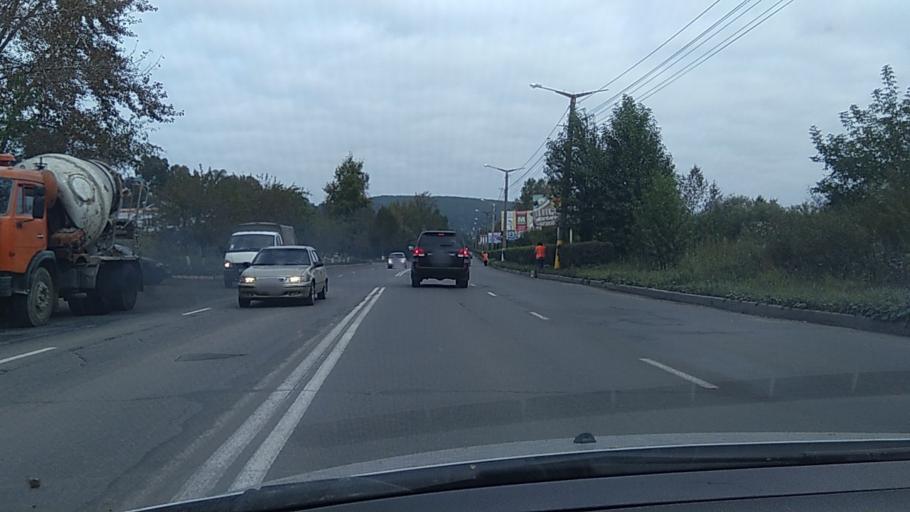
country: RU
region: Chelyabinsk
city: Zlatoust
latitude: 55.1559
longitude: 59.6796
